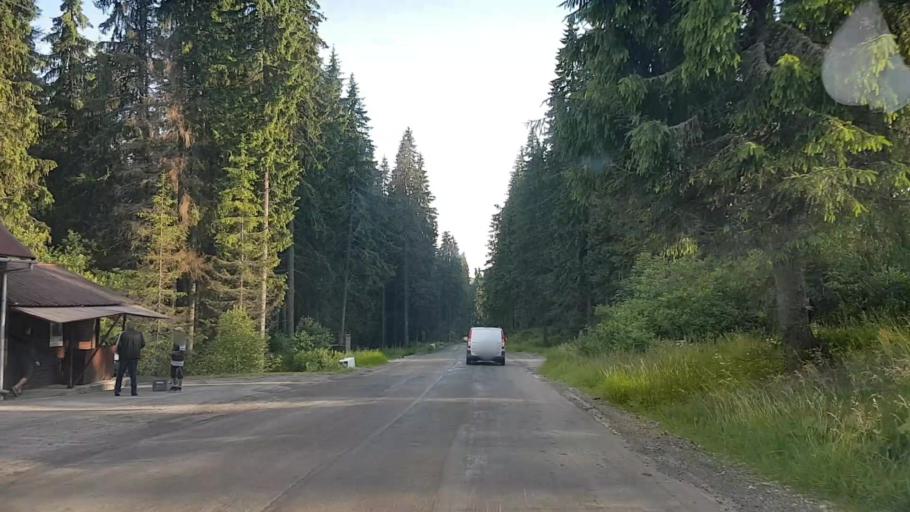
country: RO
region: Harghita
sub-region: Comuna Varsag
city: Varsag
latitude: 46.6543
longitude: 25.2925
